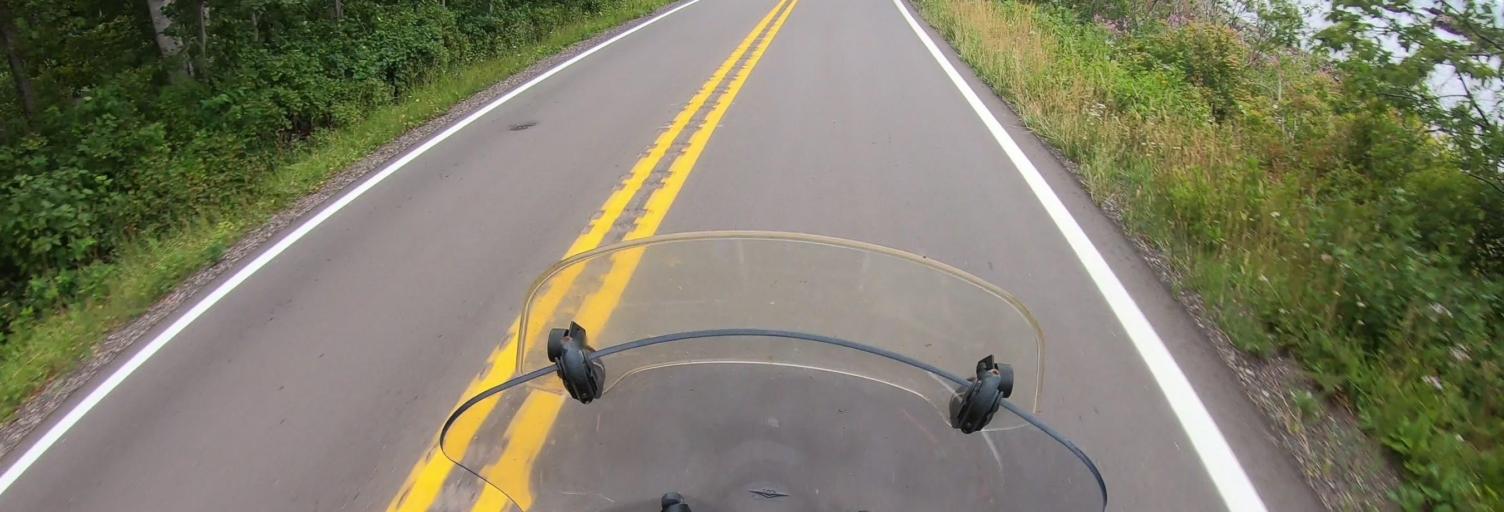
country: US
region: Michigan
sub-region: Keweenaw County
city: Eagle River
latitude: 47.4793
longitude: -87.9778
